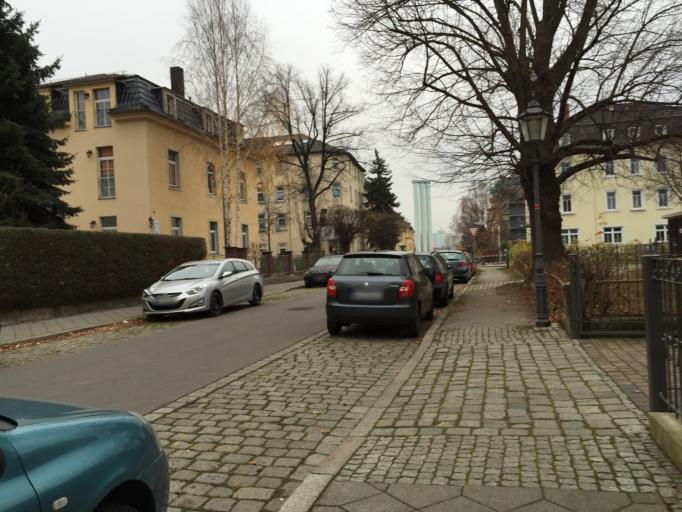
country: DE
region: Saxony
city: Dresden
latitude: 51.0408
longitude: 13.7005
